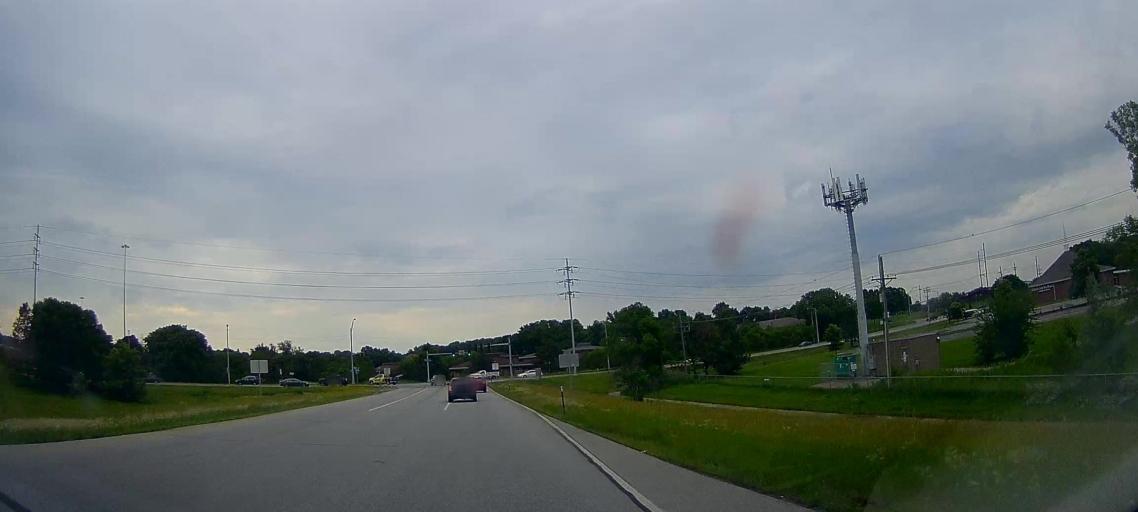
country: US
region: Nebraska
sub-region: Douglas County
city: Ralston
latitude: 41.3058
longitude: -96.0697
